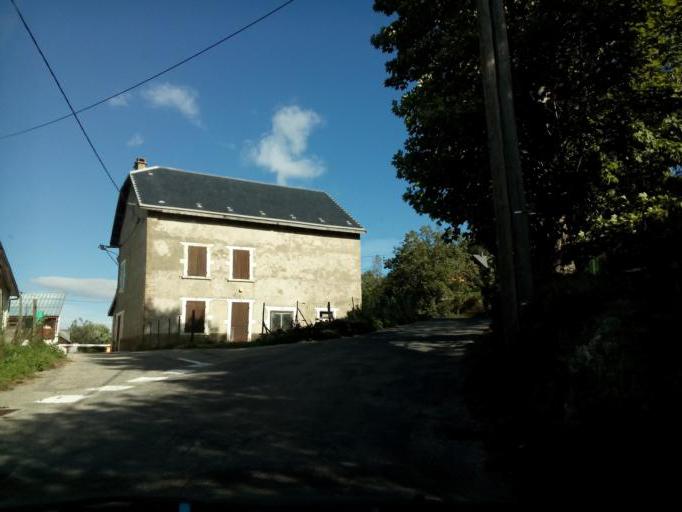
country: FR
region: Rhone-Alpes
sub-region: Departement de l'Isere
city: Vaulnaveys-le-Bas
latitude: 45.0361
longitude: 5.8506
